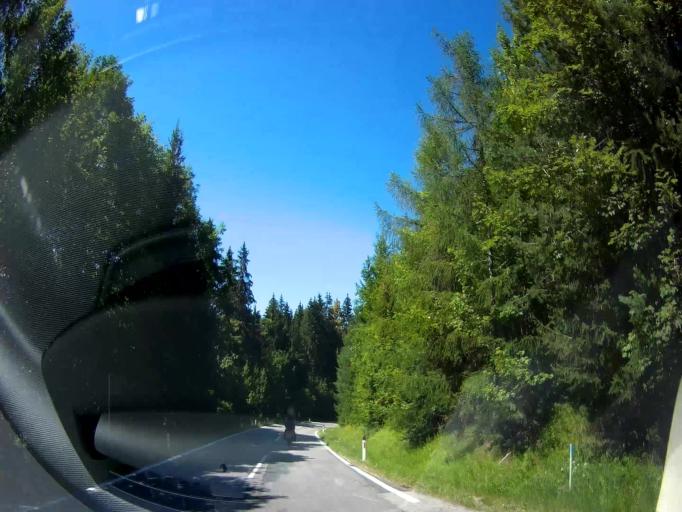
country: AT
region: Carinthia
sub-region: Politischer Bezirk Volkermarkt
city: Gallizien
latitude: 46.5403
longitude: 14.4743
